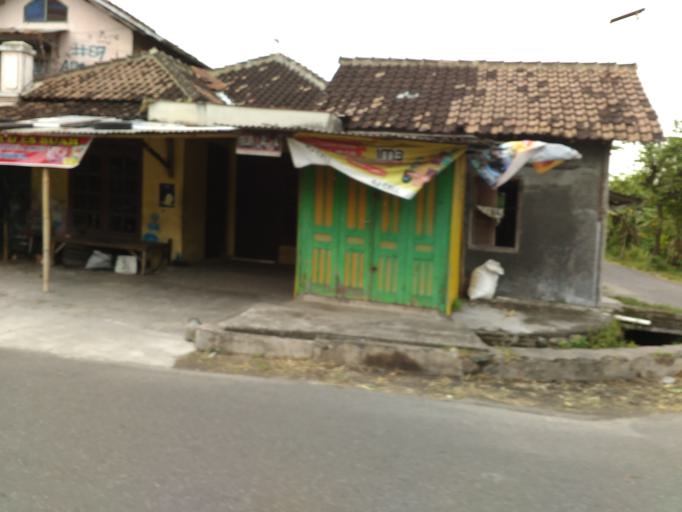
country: ID
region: Central Java
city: Delanggu
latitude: -7.5803
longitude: 110.6484
